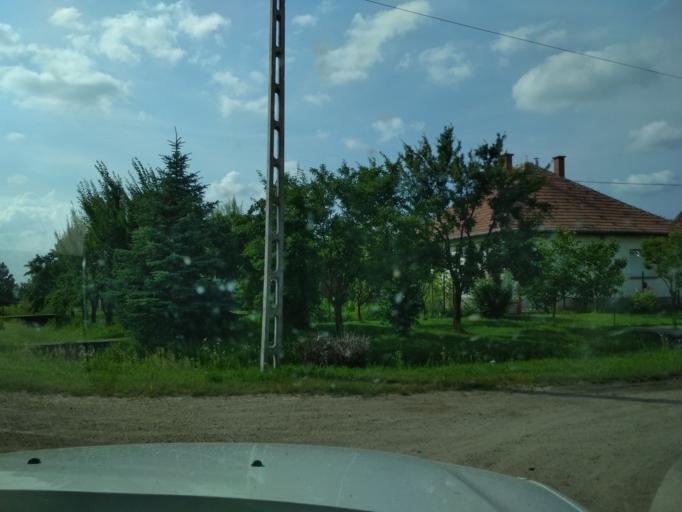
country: HU
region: Pest
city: Tapioszentmarton
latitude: 47.3325
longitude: 19.7471
